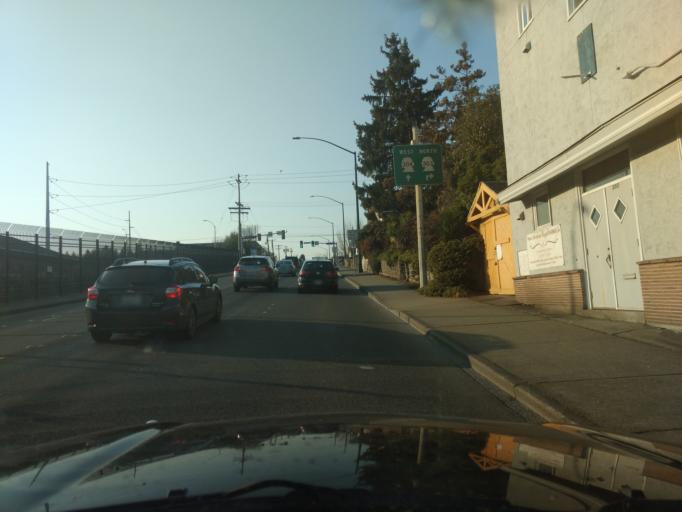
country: US
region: Washington
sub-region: Kitsap County
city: Bremerton
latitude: 47.5651
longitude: -122.6316
